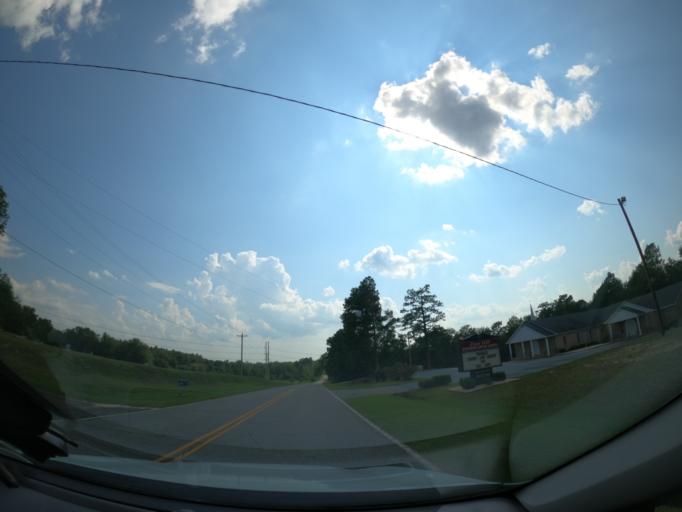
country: US
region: South Carolina
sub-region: Barnwell County
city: Williston
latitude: 33.5945
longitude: -81.4597
